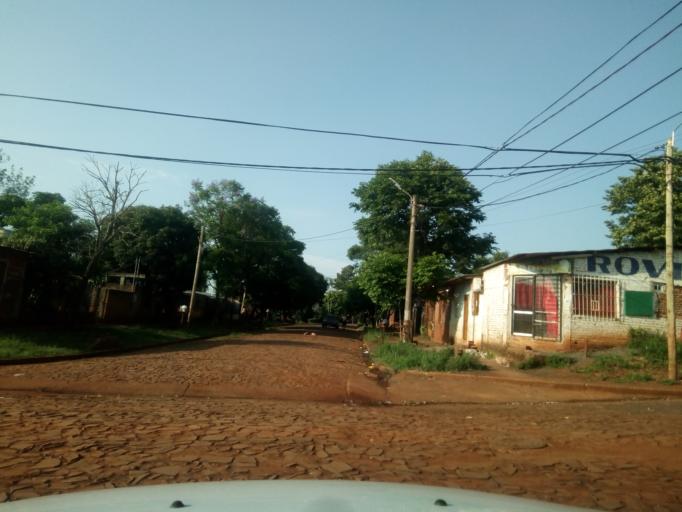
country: AR
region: Misiones
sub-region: Departamento de Capital
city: Posadas
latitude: -27.4287
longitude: -55.9122
